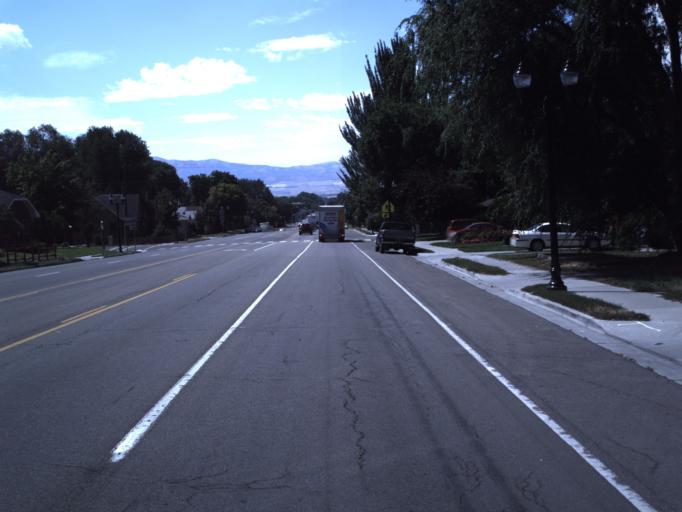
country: US
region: Utah
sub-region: Cache County
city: Logan
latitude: 41.7389
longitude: -111.8232
